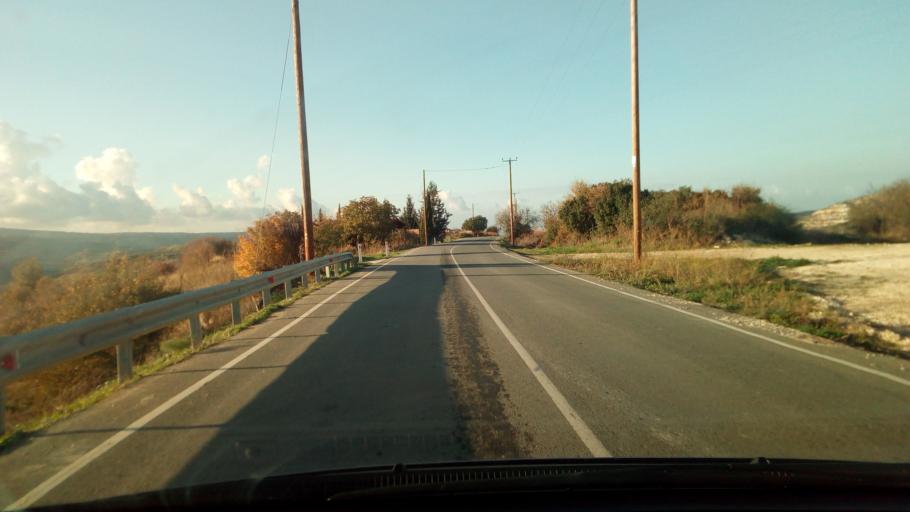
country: CY
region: Pafos
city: Polis
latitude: 34.9539
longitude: 32.4831
